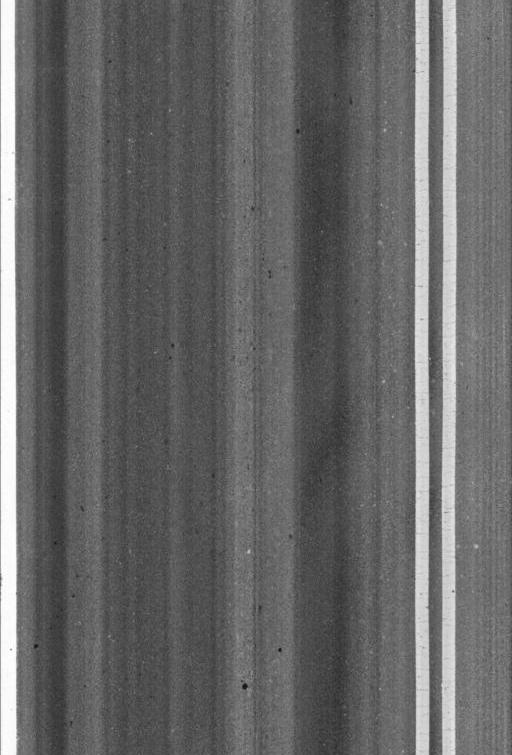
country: US
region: Washington, D.C.
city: Washington, D.C.
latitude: 38.8655
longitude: -77.0137
